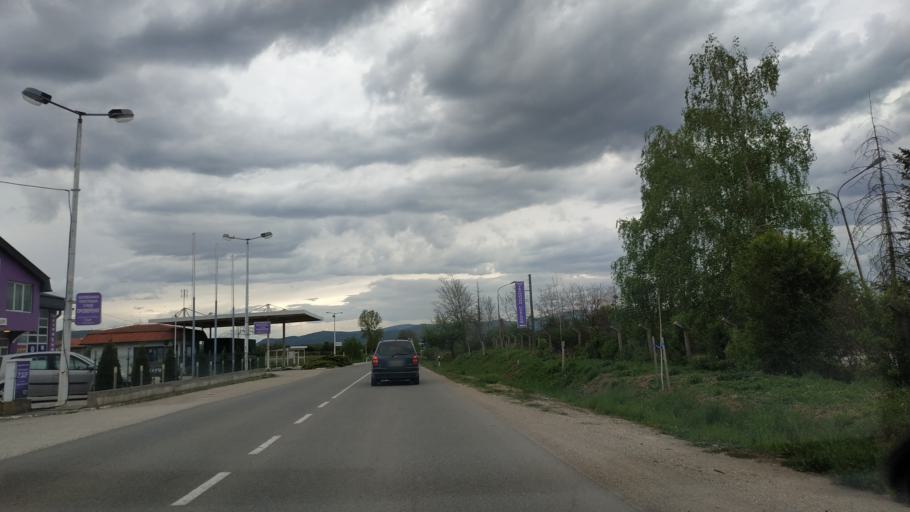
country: RS
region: Central Serbia
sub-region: Zajecarski Okrug
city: Soko Banja
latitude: 43.6523
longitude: 21.8469
